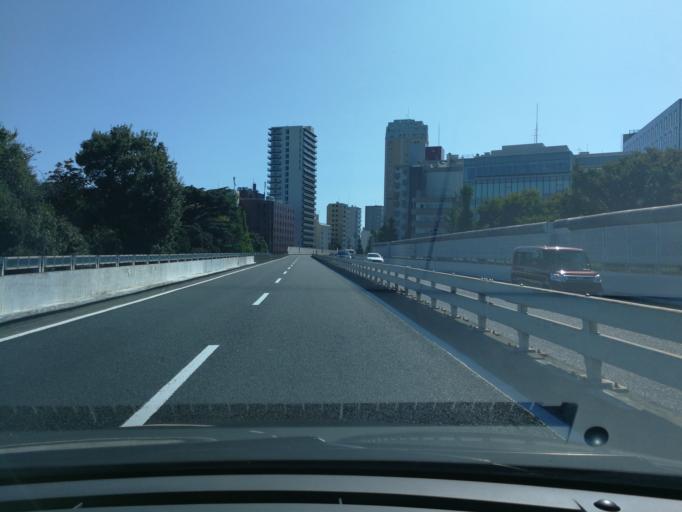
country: JP
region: Tokyo
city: Tokyo
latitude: 35.6362
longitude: 139.7180
